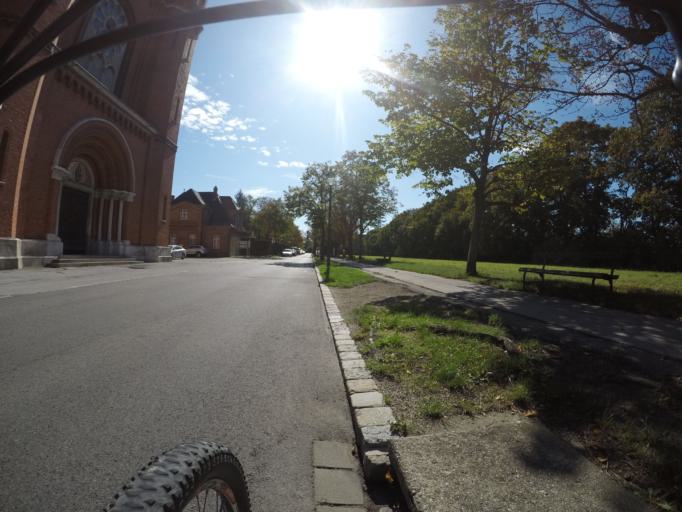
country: AT
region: Lower Austria
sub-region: Politischer Bezirk Modling
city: Modling
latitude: 48.0948
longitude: 16.2966
